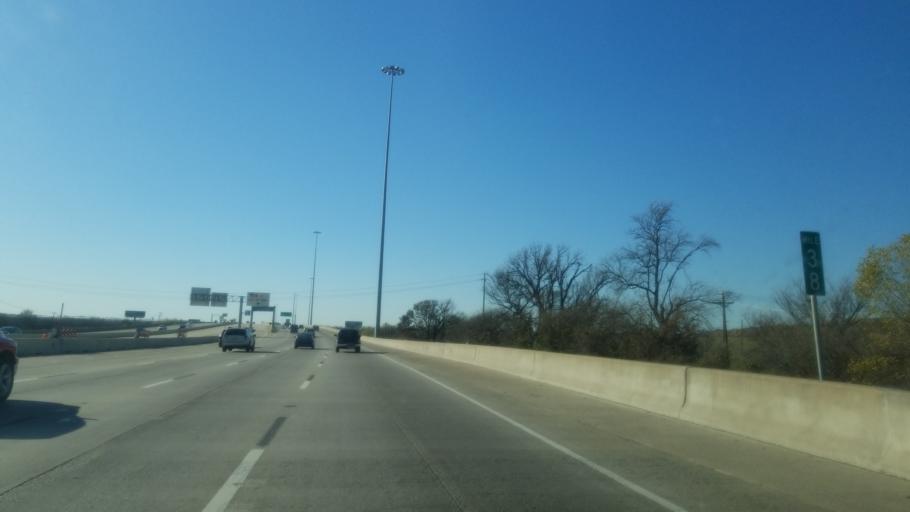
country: US
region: Texas
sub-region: Dallas County
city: Cockrell Hill
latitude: 32.7654
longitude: -96.9300
